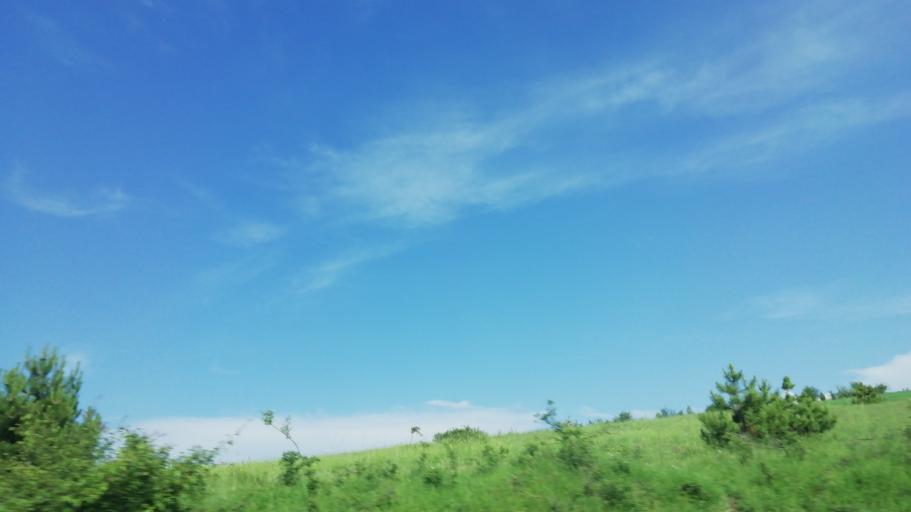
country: TR
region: Karabuk
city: Karabuk
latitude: 41.0895
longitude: 32.5875
